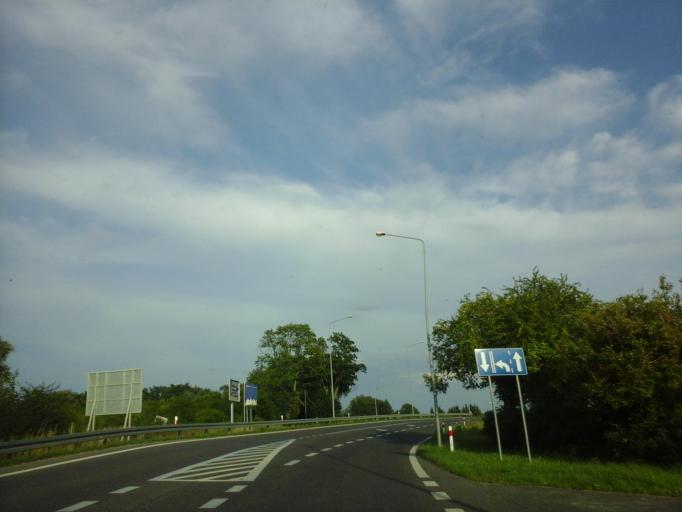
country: PL
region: West Pomeranian Voivodeship
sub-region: Powiat kamienski
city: Kamien Pomorski
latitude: 53.9631
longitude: 14.7901
